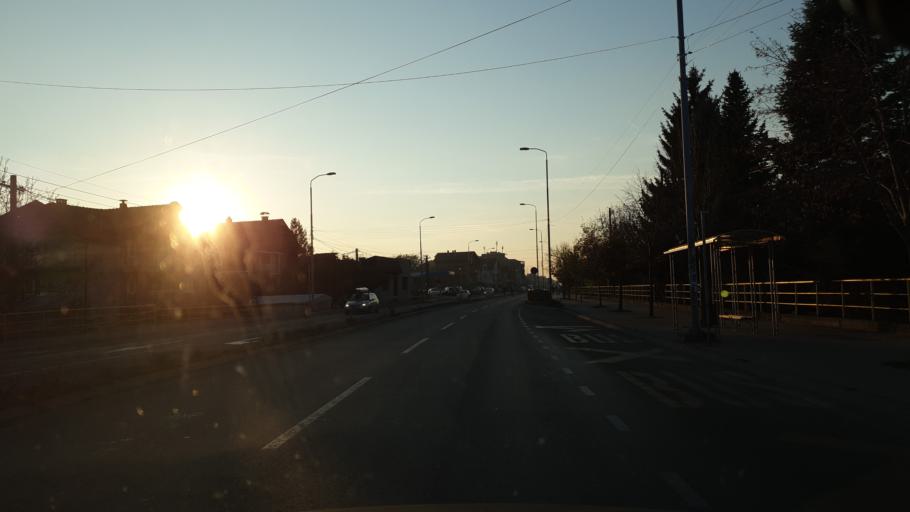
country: RS
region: Central Serbia
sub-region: Nisavski Okrug
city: Nis
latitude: 43.3301
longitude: 21.9436
